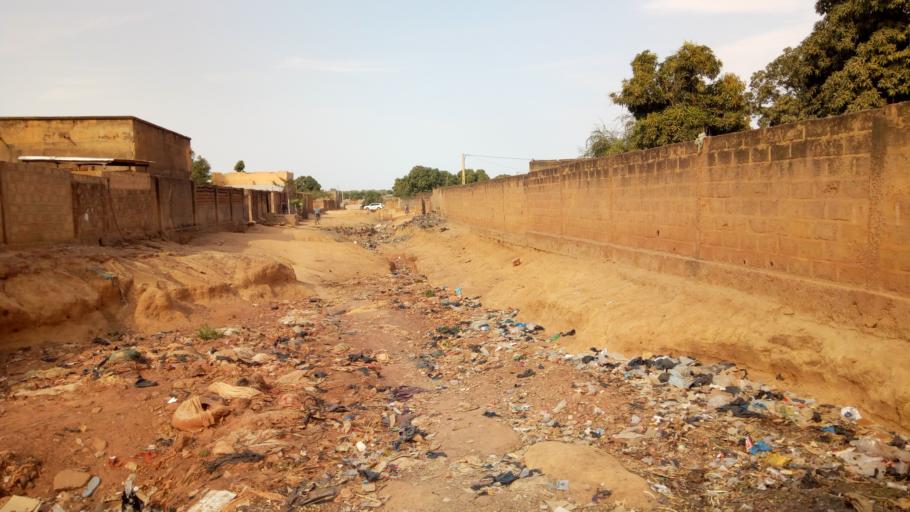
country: ML
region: Sikasso
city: Koutiala
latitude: 12.3831
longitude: -5.4834
